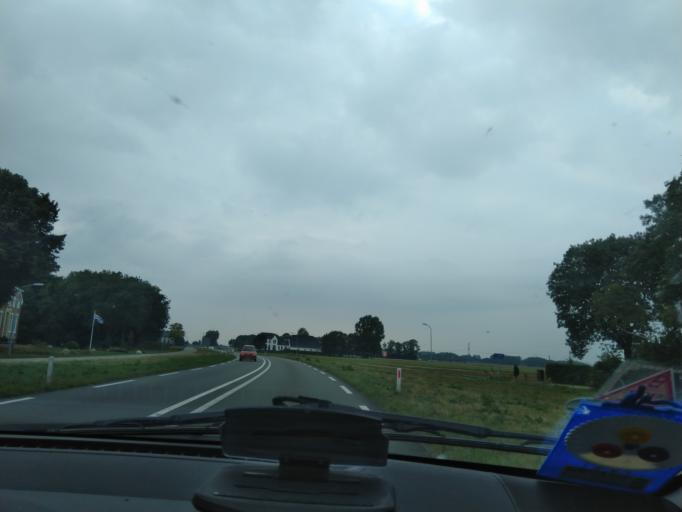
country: NL
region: Groningen
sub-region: Gemeente  Oldambt
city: Winschoten
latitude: 53.1128
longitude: 7.0640
